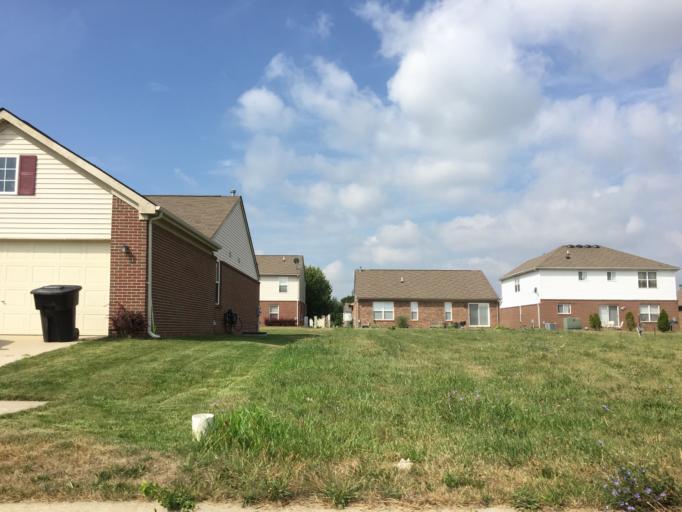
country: US
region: Michigan
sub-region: Wayne County
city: Grosse Pointe Park
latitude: 42.3632
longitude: -82.9711
